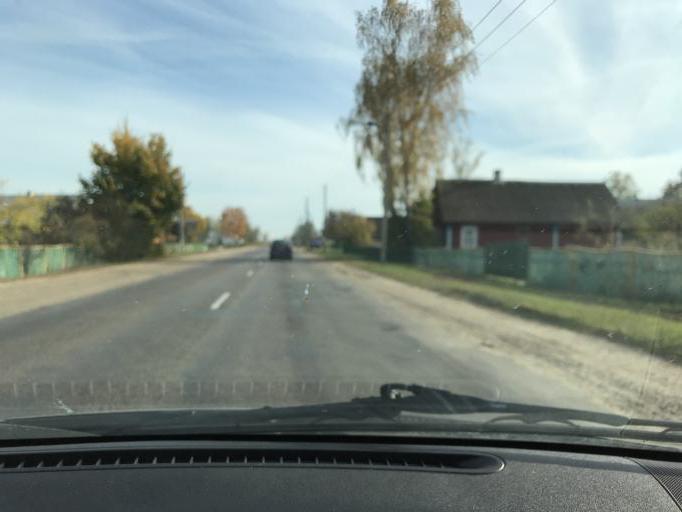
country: BY
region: Brest
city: Asnyezhytsy
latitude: 52.2264
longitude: 26.0244
